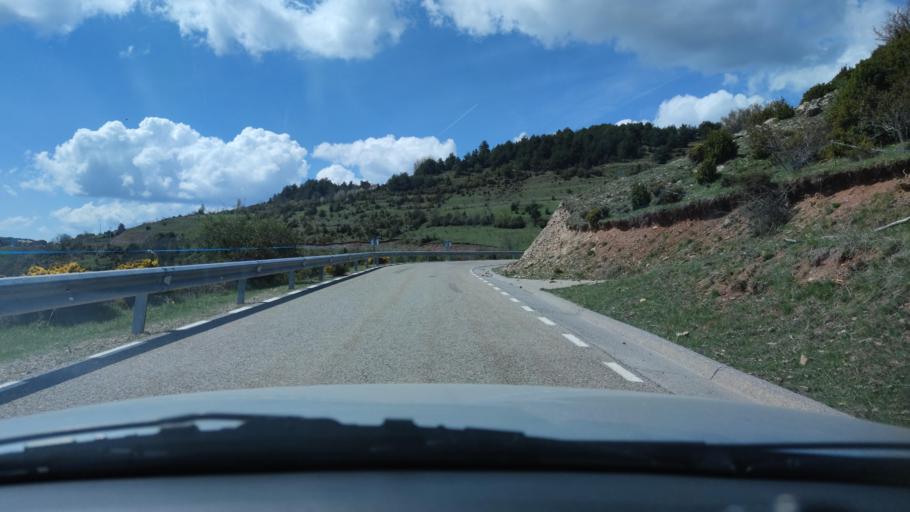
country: ES
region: Catalonia
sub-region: Provincia de Lleida
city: Coll de Nargo
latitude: 42.2926
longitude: 1.2315
